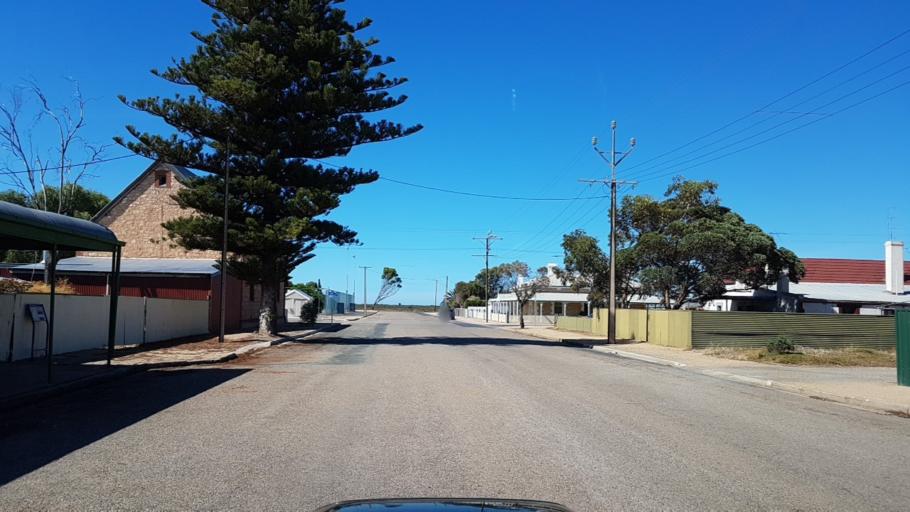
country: AU
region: South Australia
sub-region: Wakefield
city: Balaklava
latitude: -34.1857
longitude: 138.1485
